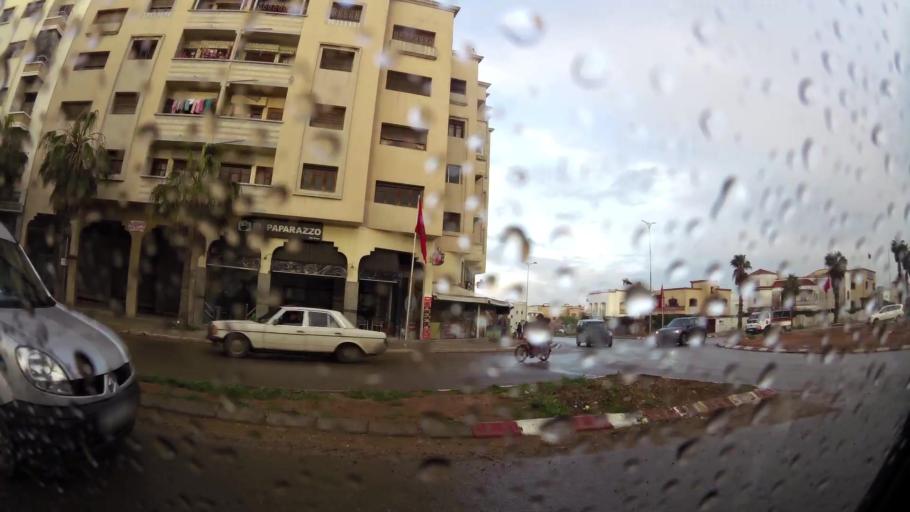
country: MA
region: Doukkala-Abda
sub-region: El-Jadida
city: El Jadida
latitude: 33.2265
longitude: -8.4934
